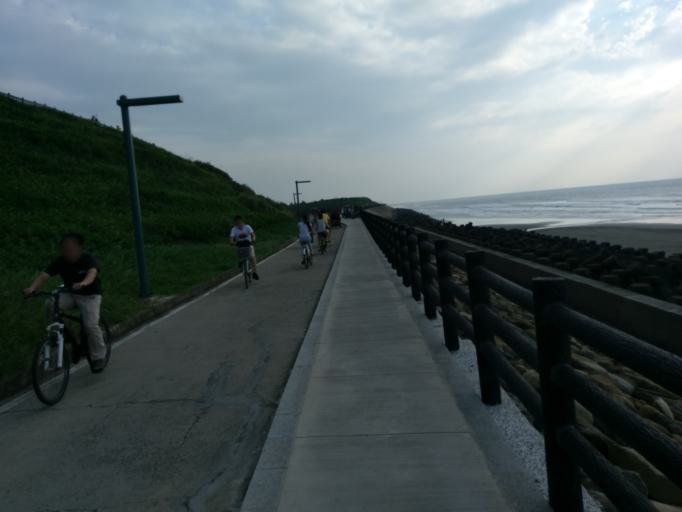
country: TW
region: Taiwan
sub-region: Hsinchu
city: Hsinchu
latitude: 24.8326
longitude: 120.9145
